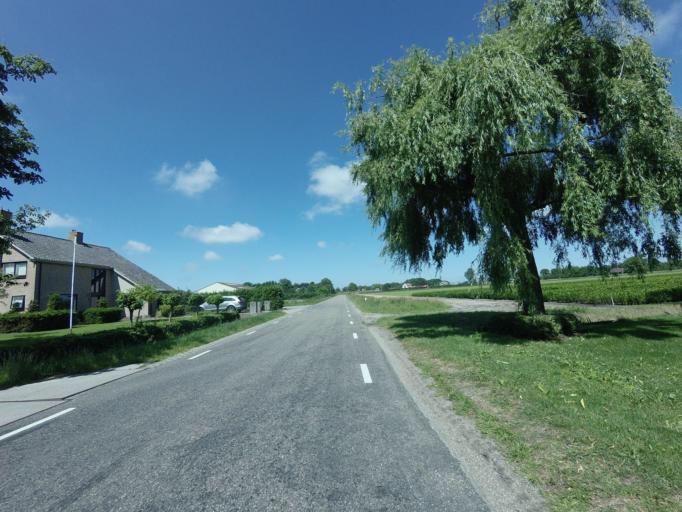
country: NL
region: North Holland
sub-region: Gemeente Den Helder
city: Den Helder
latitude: 52.8885
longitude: 4.8192
